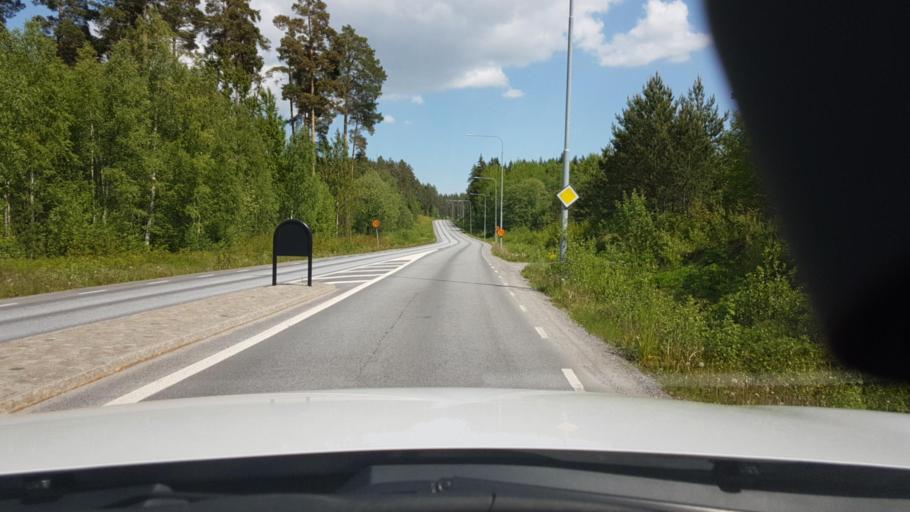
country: SE
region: Stockholm
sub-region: Vallentuna Kommun
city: Vallentuna
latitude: 59.4976
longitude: 18.0915
